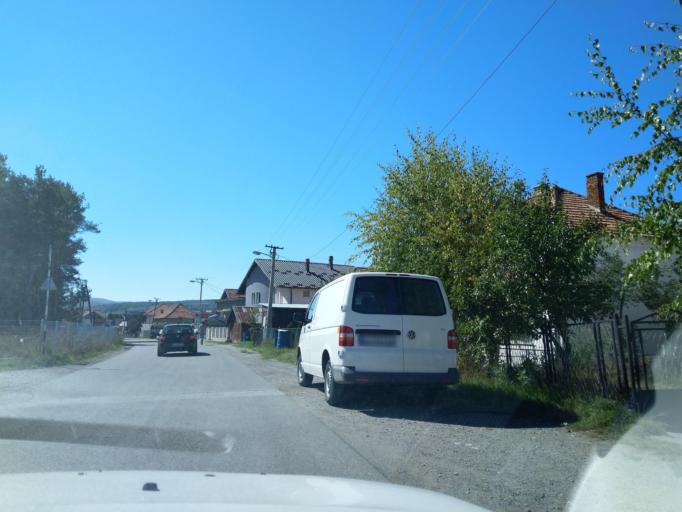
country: RS
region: Central Serbia
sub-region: Zlatiborski Okrug
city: Sjenica
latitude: 43.2733
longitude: 20.0098
